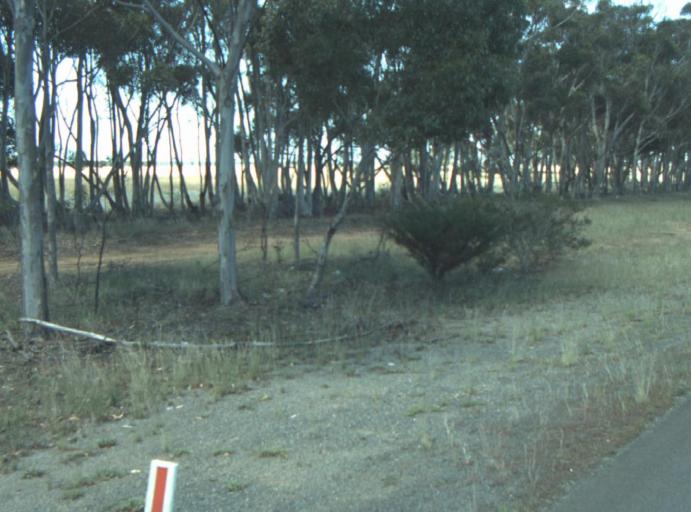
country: AU
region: Victoria
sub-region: Greater Geelong
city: Lara
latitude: -37.9391
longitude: 144.3581
